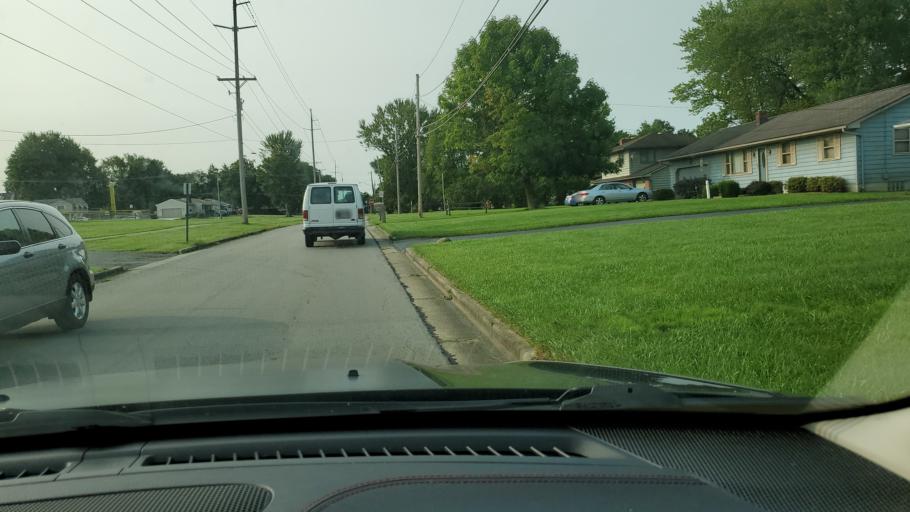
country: US
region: Ohio
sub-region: Mahoning County
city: Poland
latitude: 41.0349
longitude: -80.6212
